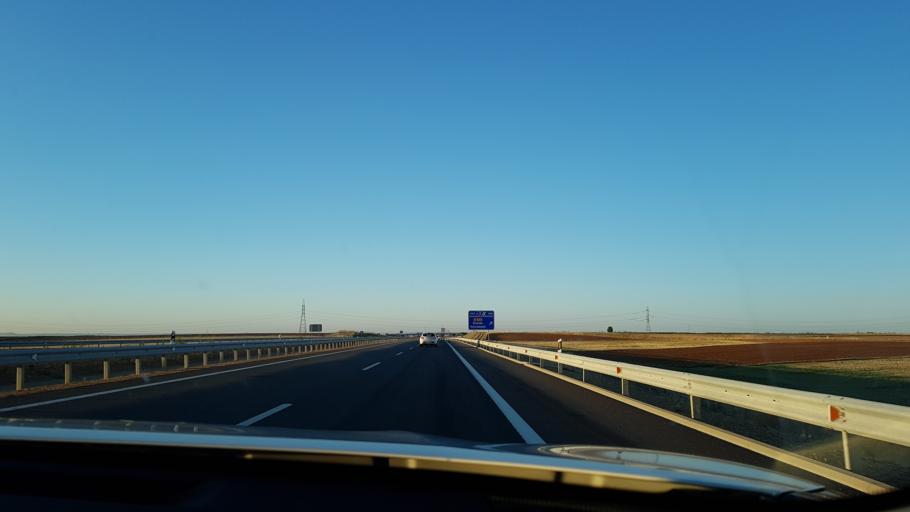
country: ES
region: Castille and Leon
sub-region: Provincia de Zamora
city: Roales
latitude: 41.5869
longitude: -5.7782
